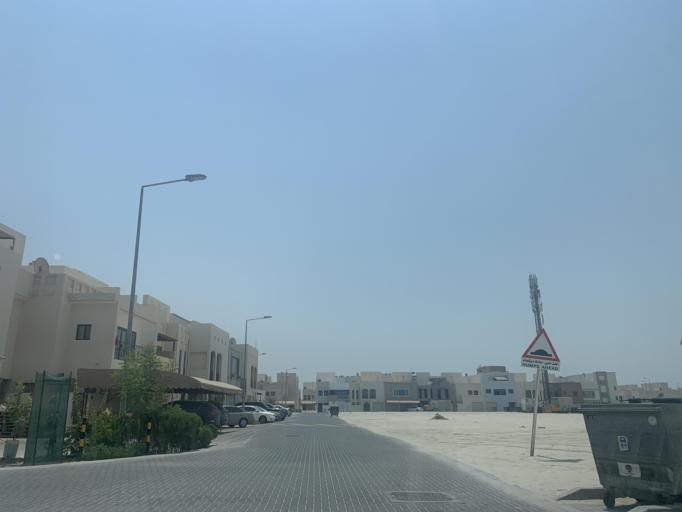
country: BH
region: Muharraq
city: Al Hadd
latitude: 26.2370
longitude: 50.6715
